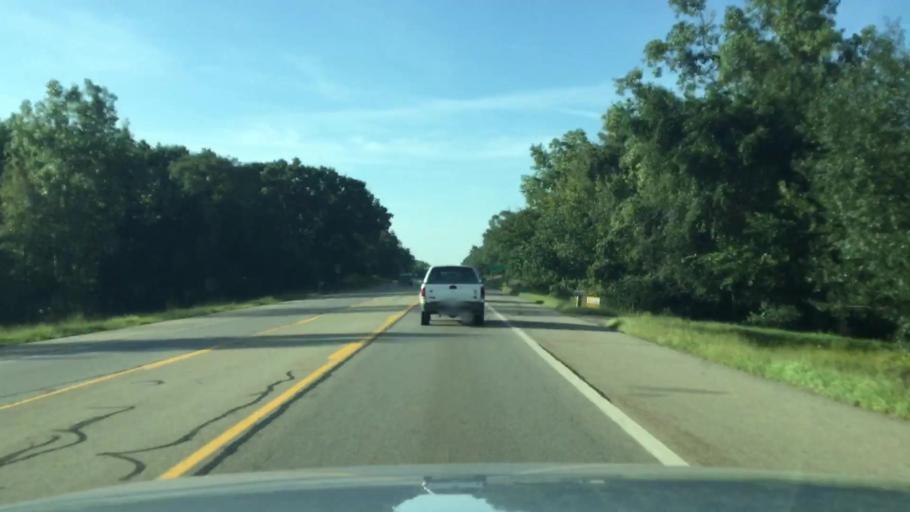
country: US
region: Michigan
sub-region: Jackson County
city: Vandercook Lake
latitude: 42.1722
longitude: -84.3647
